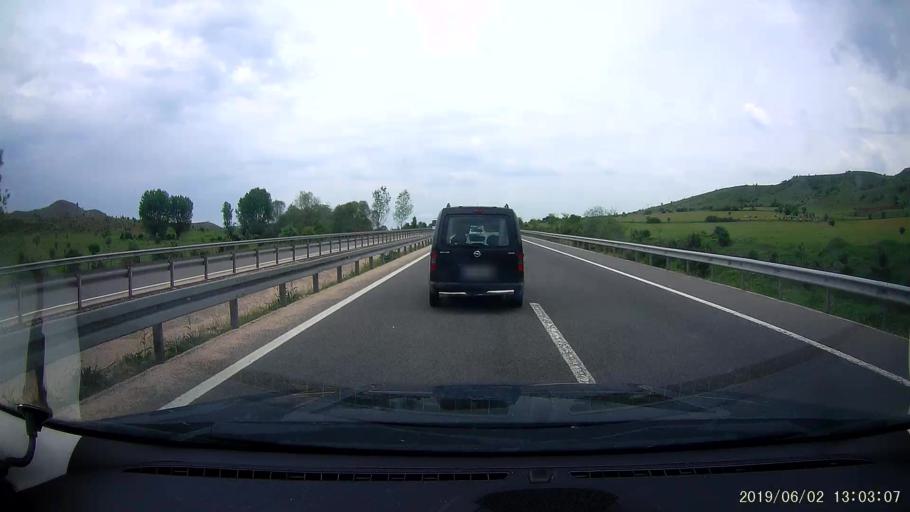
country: TR
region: Karabuk
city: Gozyeri
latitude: 40.8586
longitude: 32.4950
